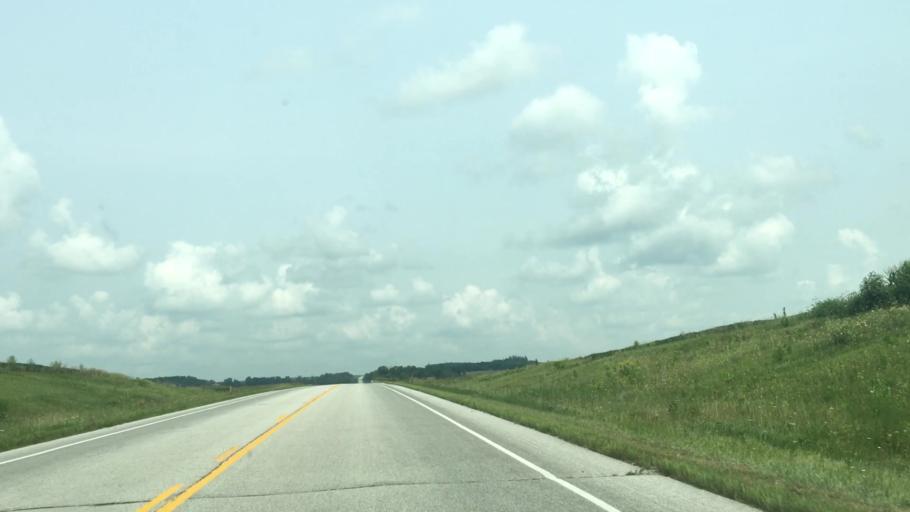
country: US
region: Minnesota
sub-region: Fillmore County
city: Harmony
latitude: 43.6179
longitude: -91.9298
